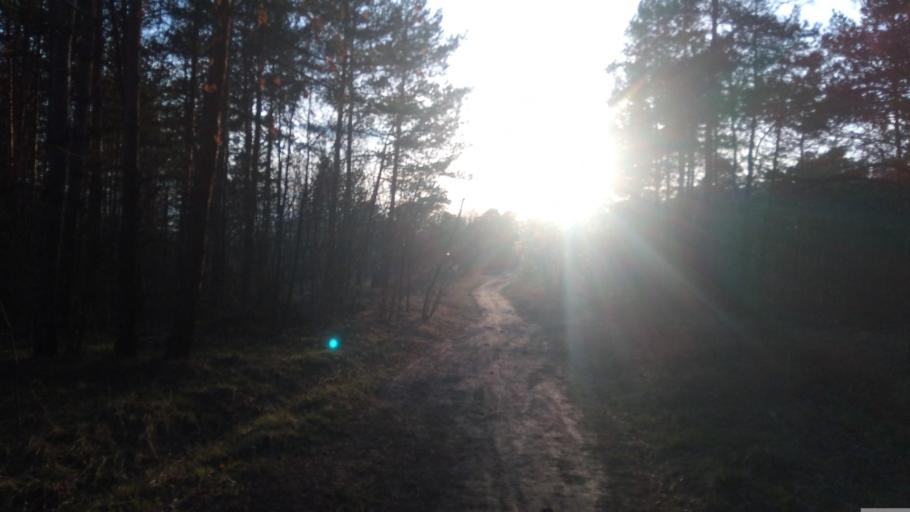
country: RU
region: Chelyabinsk
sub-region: Gorod Chelyabinsk
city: Chelyabinsk
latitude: 55.1590
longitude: 61.3264
